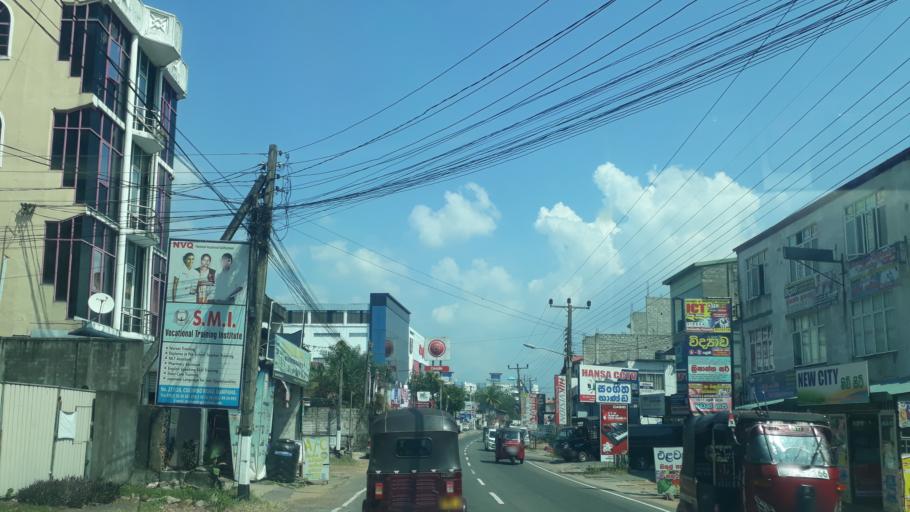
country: LK
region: Western
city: Gampaha
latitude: 7.0900
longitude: 80.0033
